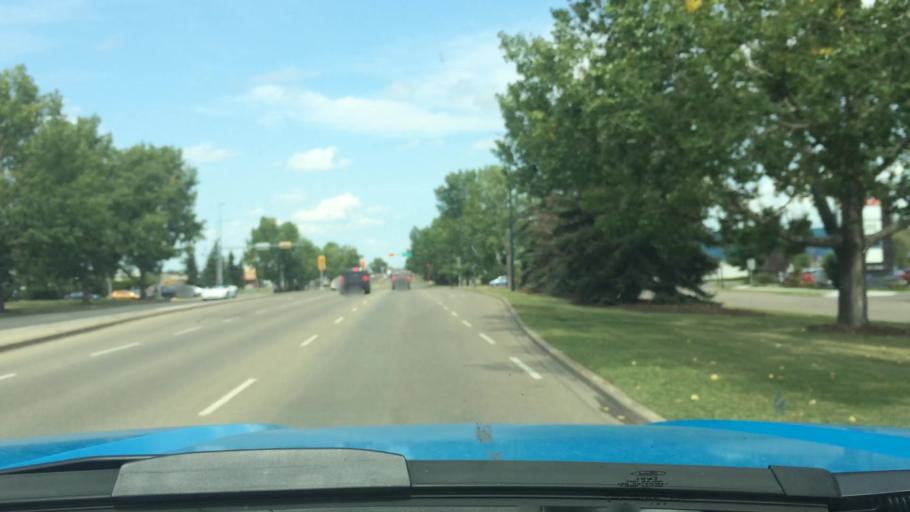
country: CA
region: Alberta
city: Red Deer
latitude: 52.2377
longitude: -113.8139
